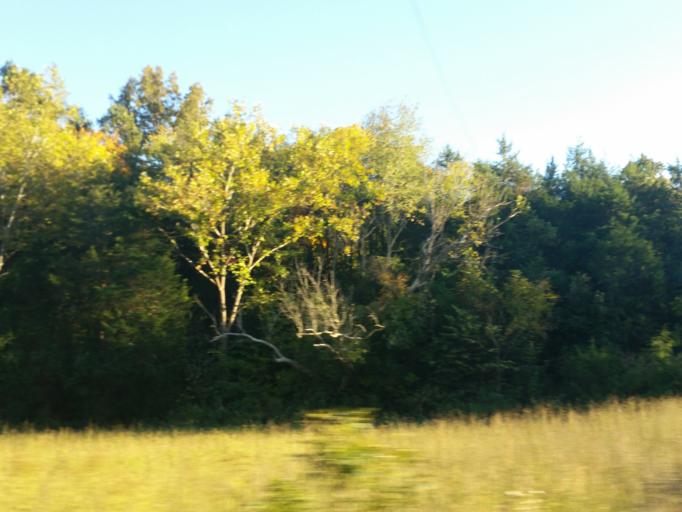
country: US
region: Tennessee
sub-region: Grainger County
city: Rutledge
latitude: 36.3365
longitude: -83.4939
